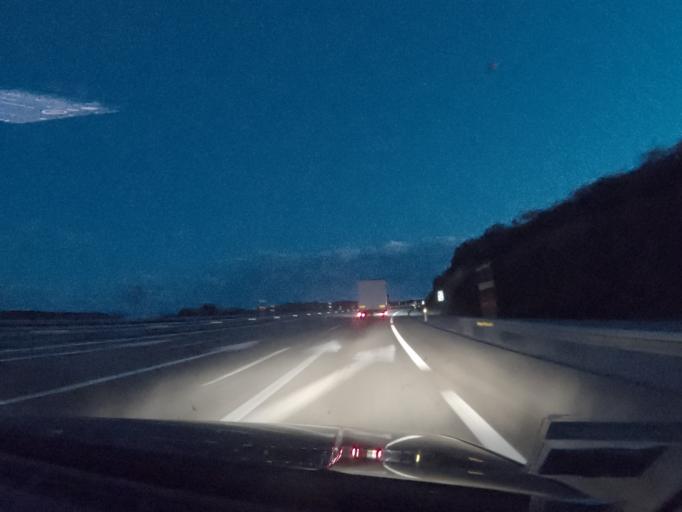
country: ES
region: Castille and Leon
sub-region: Provincia de Leon
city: Villagaton
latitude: 42.5872
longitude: -6.2152
